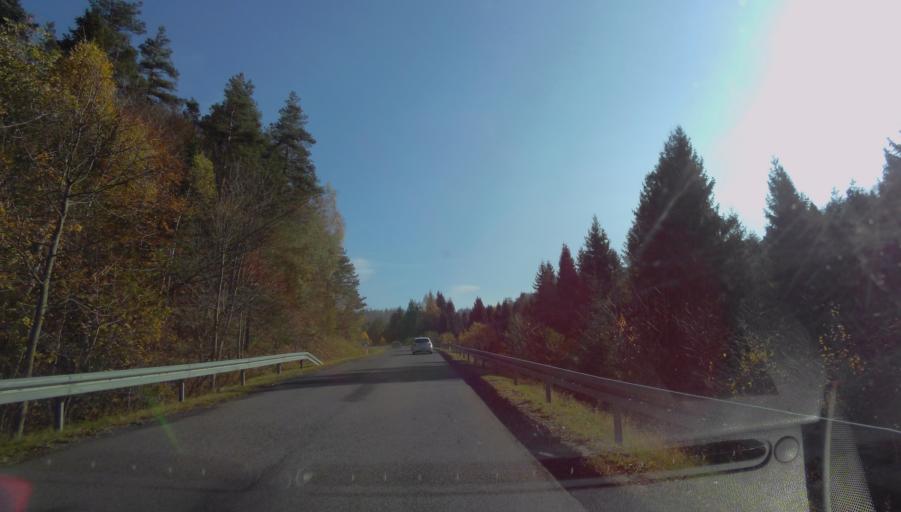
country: PL
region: Subcarpathian Voivodeship
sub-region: Powiat leski
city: Cisna
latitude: 49.2175
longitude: 22.2262
